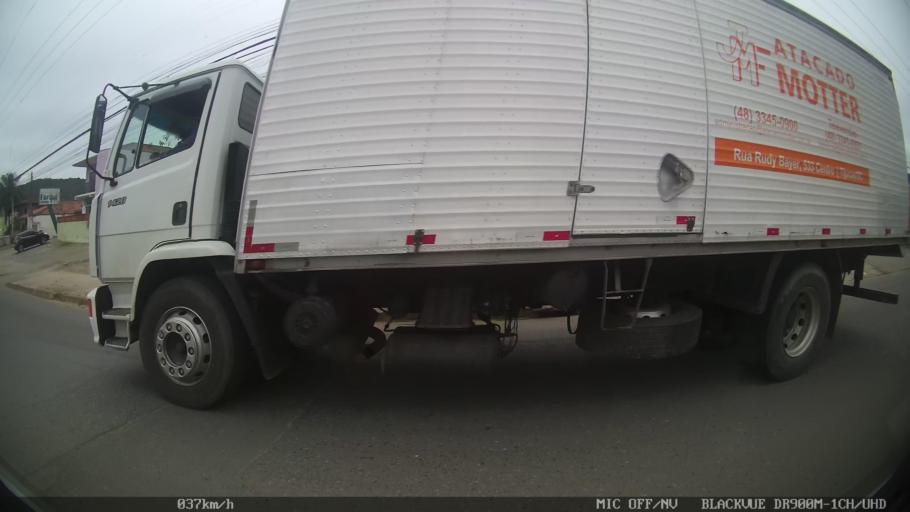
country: BR
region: Santa Catarina
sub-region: Joinville
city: Joinville
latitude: -26.3619
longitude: -48.8149
